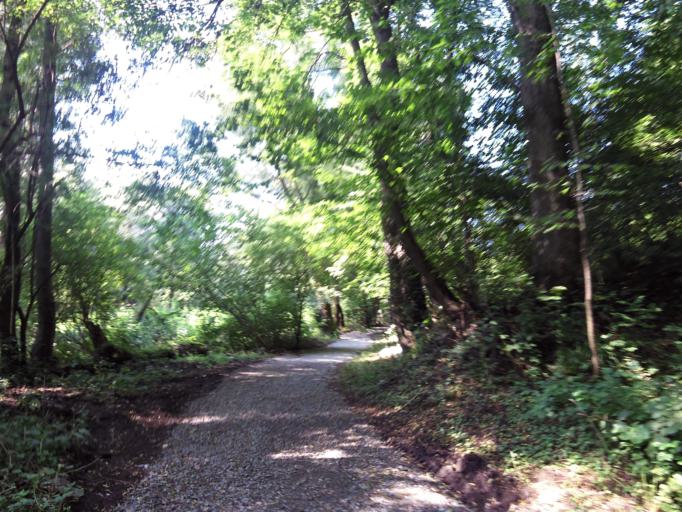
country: PL
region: Silesian Voivodeship
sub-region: Powiat zywiecki
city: Wieprz
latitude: 49.6562
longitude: 19.1814
